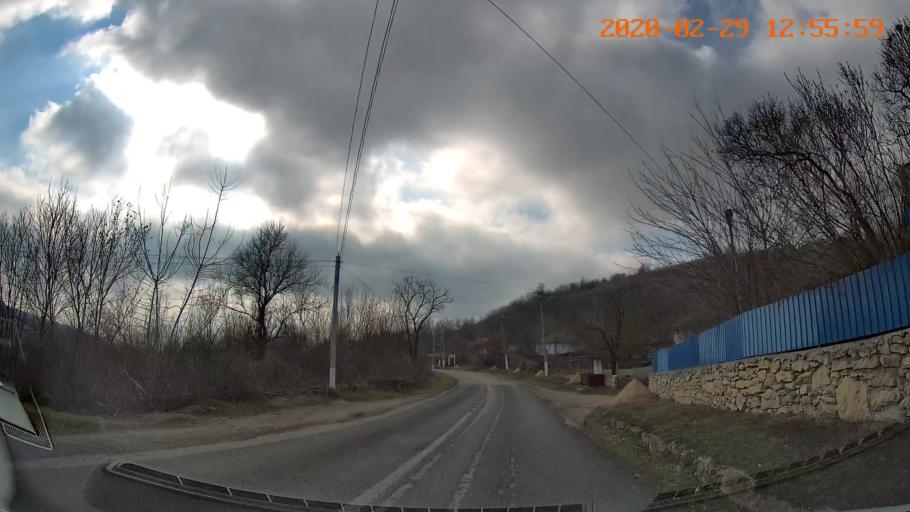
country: MD
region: Telenesti
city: Camenca
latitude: 48.0906
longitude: 28.7241
